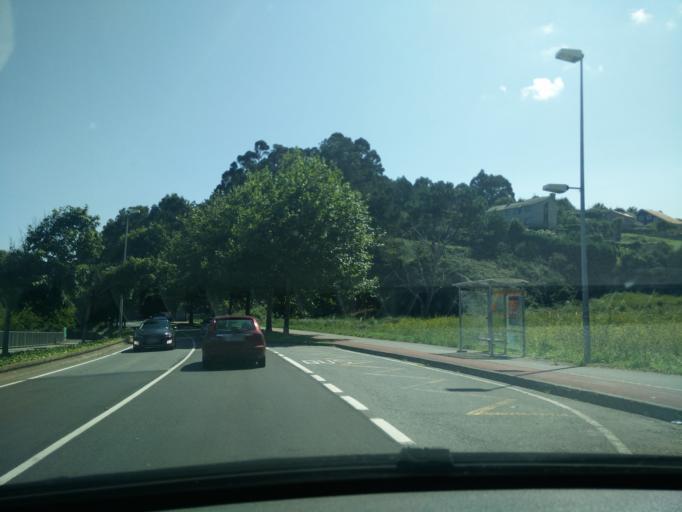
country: ES
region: Galicia
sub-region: Provincia da Coruna
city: A Coruna
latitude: 43.3394
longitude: -8.3648
